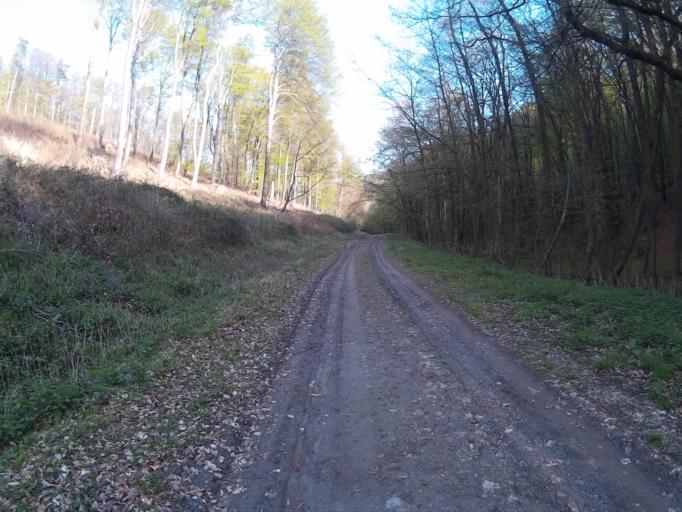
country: AT
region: Burgenland
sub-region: Politischer Bezirk Oberwart
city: Rechnitz
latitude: 47.3383
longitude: 16.4725
